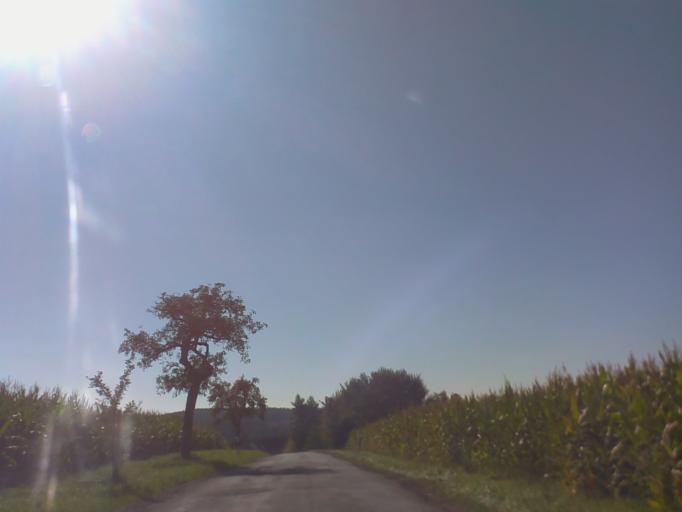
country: DE
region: Thuringia
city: Unterbodnitz
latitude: 50.8062
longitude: 11.6484
